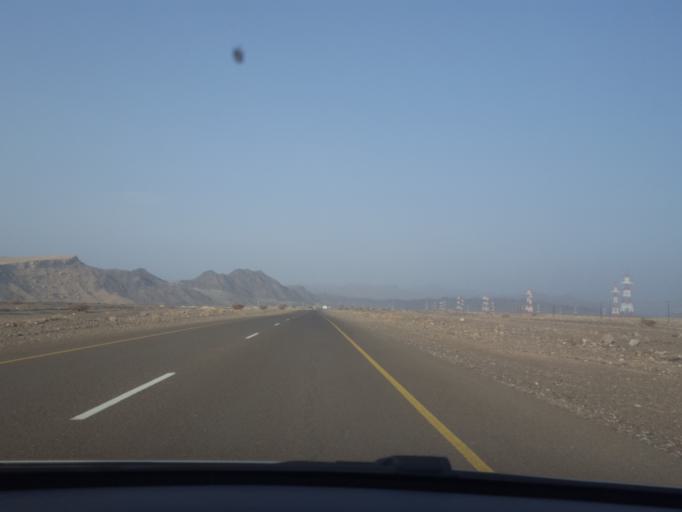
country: AE
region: Abu Dhabi
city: Al Ain
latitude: 24.0441
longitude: 56.0341
